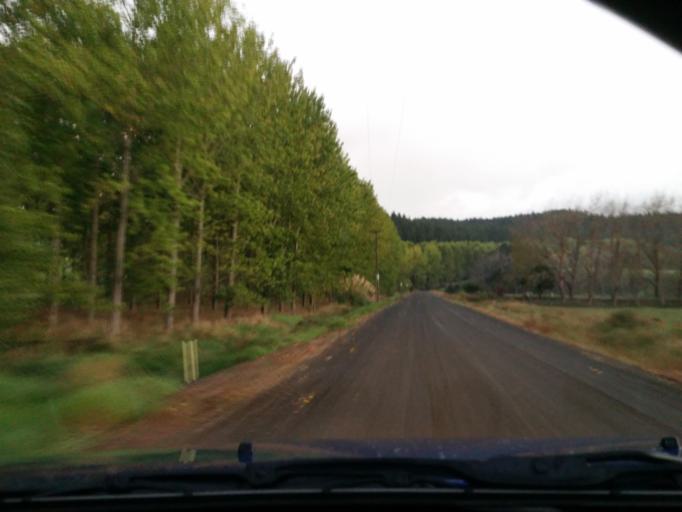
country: NZ
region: Northland
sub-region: Whangarei
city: Maungatapere
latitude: -35.8182
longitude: 174.0399
